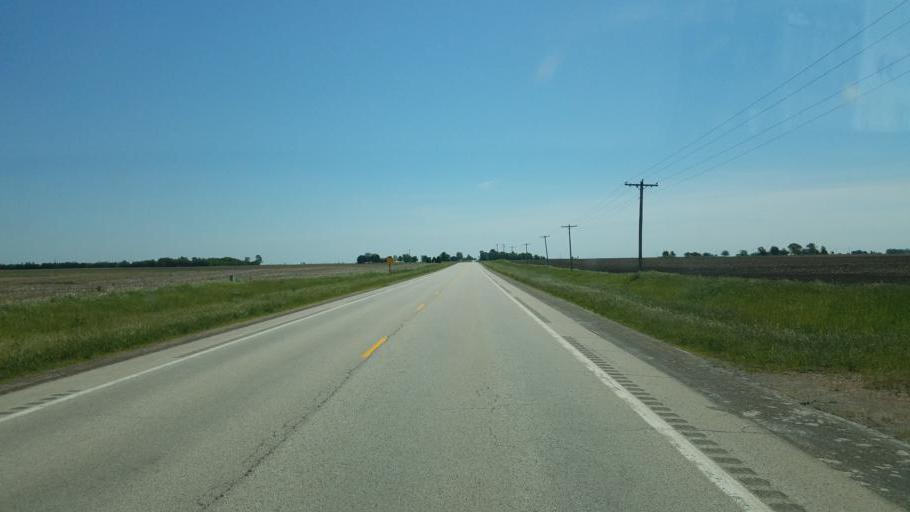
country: US
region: Illinois
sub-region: McLean County
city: Heyworth
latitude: 40.3123
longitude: -88.9301
